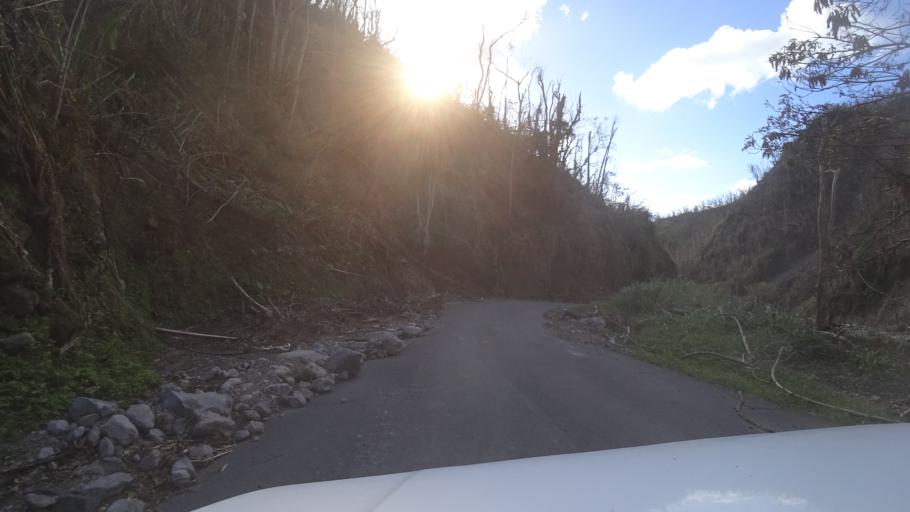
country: DM
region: Saint Luke
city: Pointe Michel
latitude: 15.2749
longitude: -61.3586
